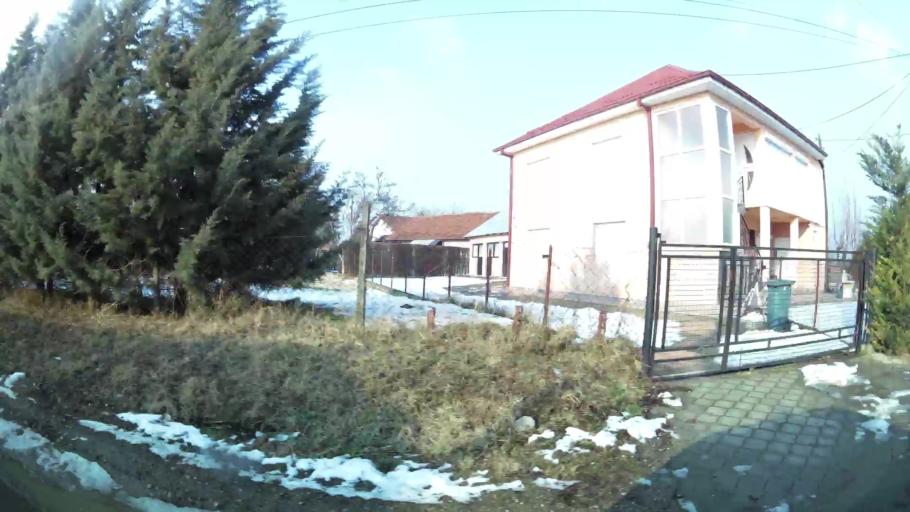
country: MK
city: Kadino
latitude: 41.9703
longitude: 21.5988
